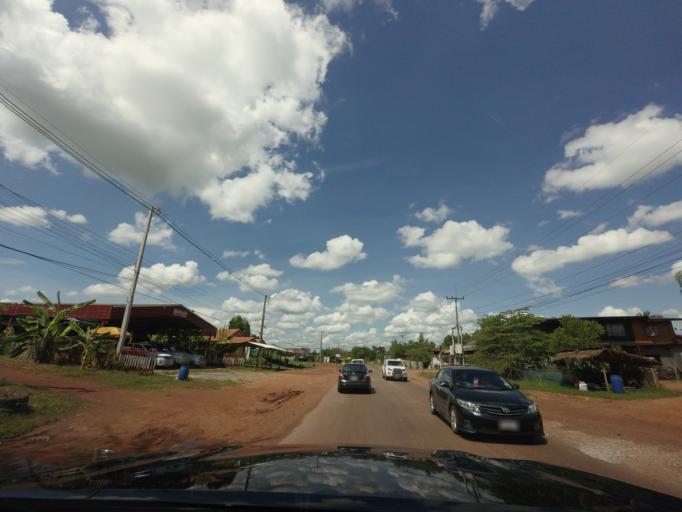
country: TH
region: Changwat Udon Thani
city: Ban Dung
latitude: 17.7341
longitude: 103.2530
